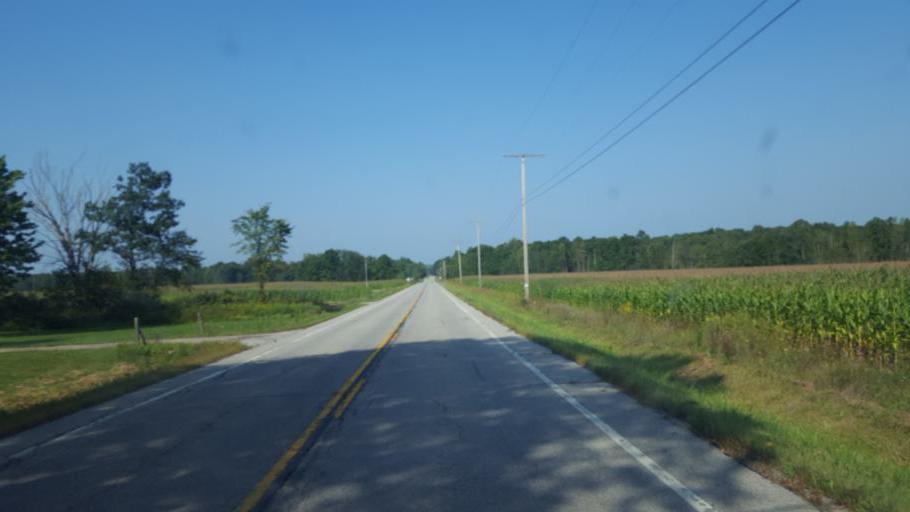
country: US
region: Ohio
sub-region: Ashtabula County
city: Roaming Shores
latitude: 41.6054
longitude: -80.8740
